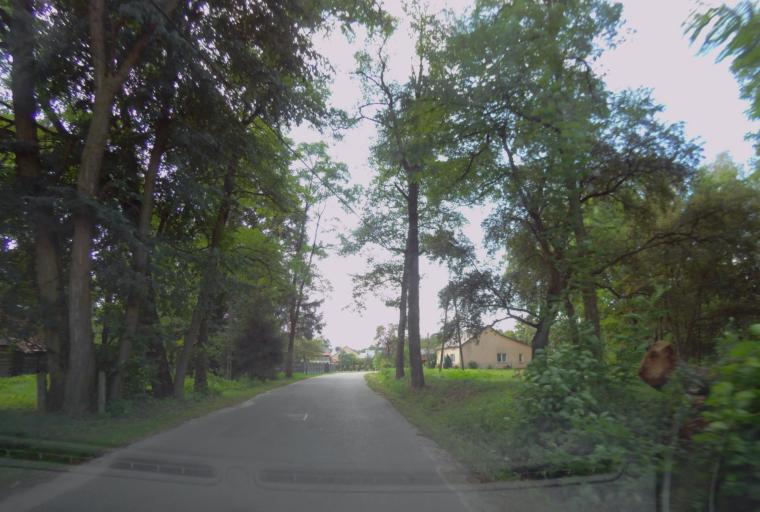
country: PL
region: Subcarpathian Voivodeship
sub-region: Powiat nizanski
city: Jezowe
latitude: 50.3885
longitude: 22.1084
